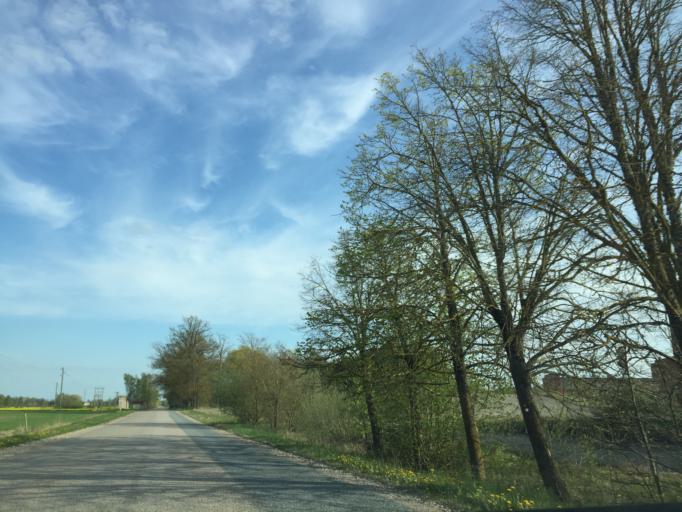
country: LV
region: Bauskas Rajons
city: Bauska
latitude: 56.3392
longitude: 24.2376
